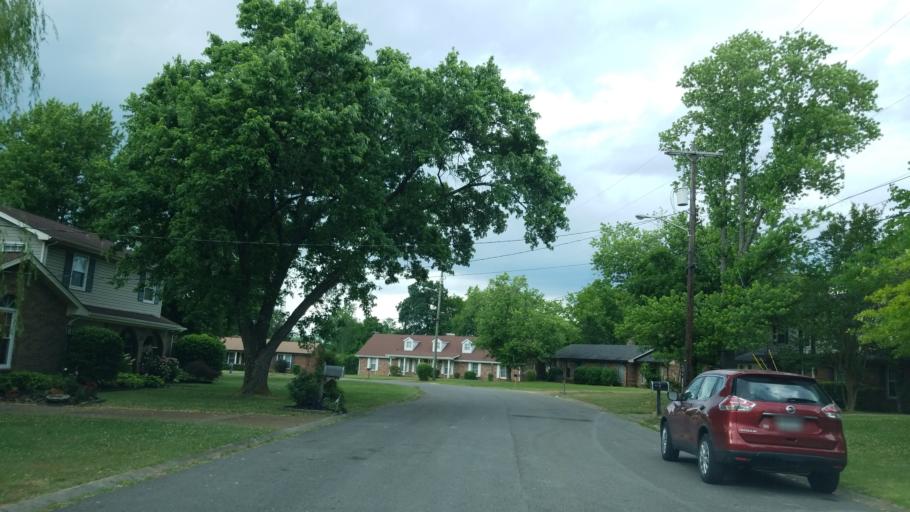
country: US
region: Tennessee
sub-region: Rutherford County
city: La Vergne
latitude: 36.0972
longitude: -86.6071
